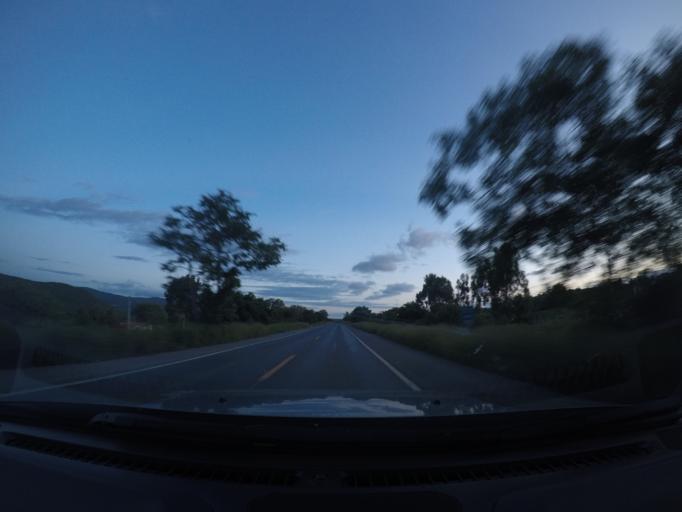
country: BR
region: Bahia
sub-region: Seabra
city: Seabra
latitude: -12.4772
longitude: -41.7401
